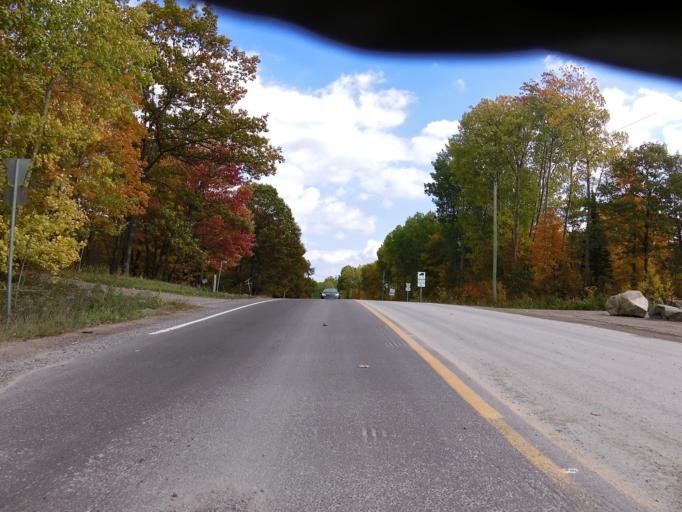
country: CA
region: Ontario
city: Petawawa
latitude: 45.8097
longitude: -77.3490
